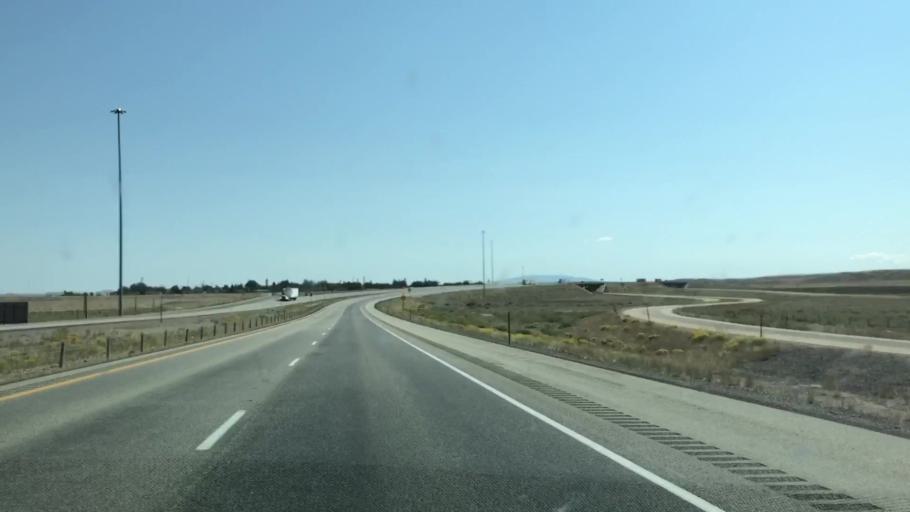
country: US
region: Wyoming
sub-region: Carbon County
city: Rawlins
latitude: 41.7813
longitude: -107.1342
